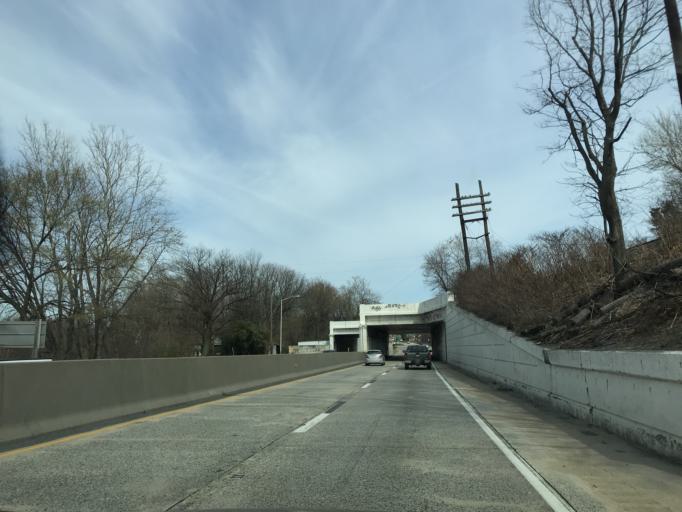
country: US
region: Pennsylvania
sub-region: Perry County
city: Marysville
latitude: 40.3614
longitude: -76.9260
